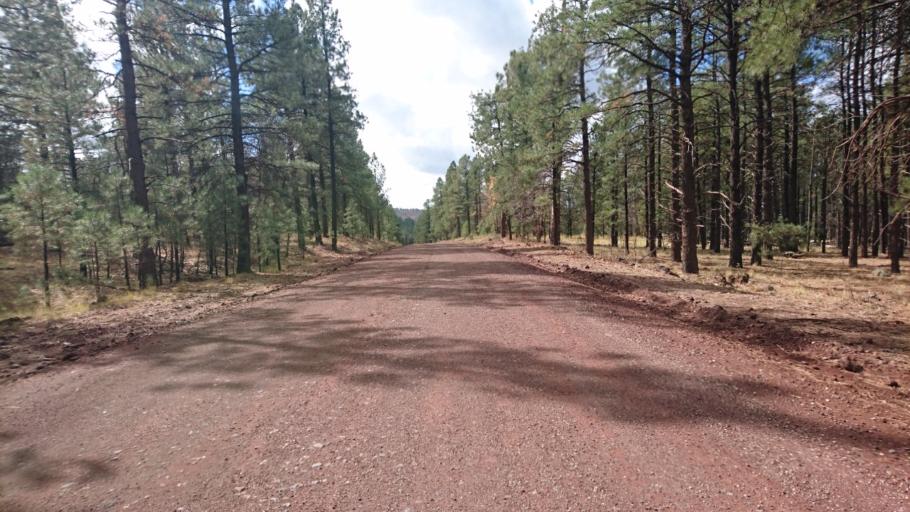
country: US
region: Arizona
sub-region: Coconino County
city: Parks
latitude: 35.2703
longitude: -111.9092
